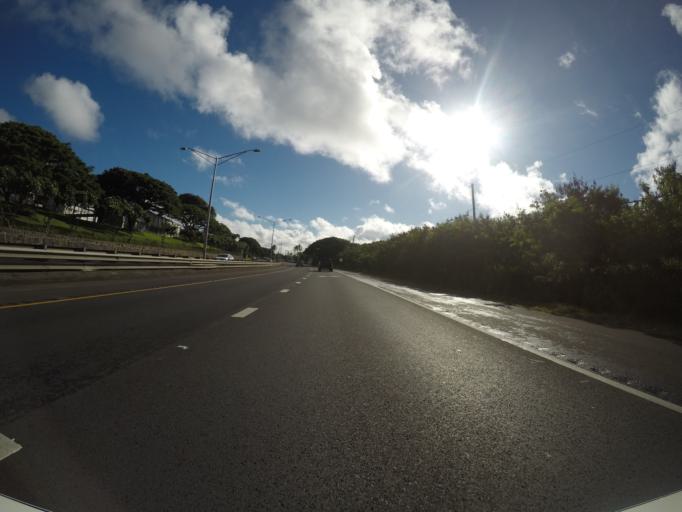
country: US
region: Hawaii
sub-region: Honolulu County
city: Kailua
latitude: 21.4076
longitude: -157.7568
